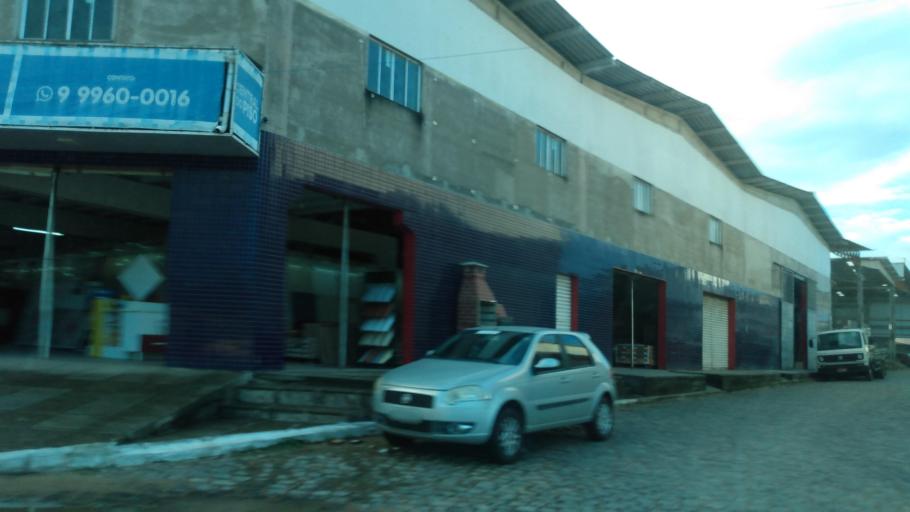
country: BR
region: Pernambuco
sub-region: Palmares
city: Palmares
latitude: -8.6791
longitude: -35.5788
